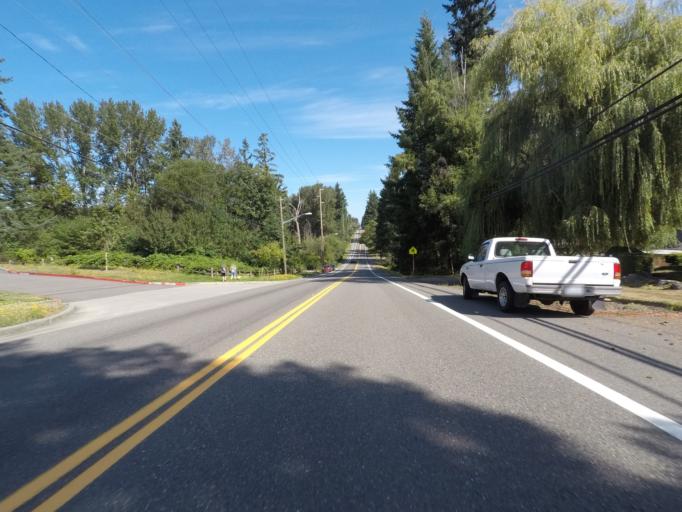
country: US
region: Washington
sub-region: King County
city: Inglewood-Finn Hill
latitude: 47.7207
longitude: -122.2294
